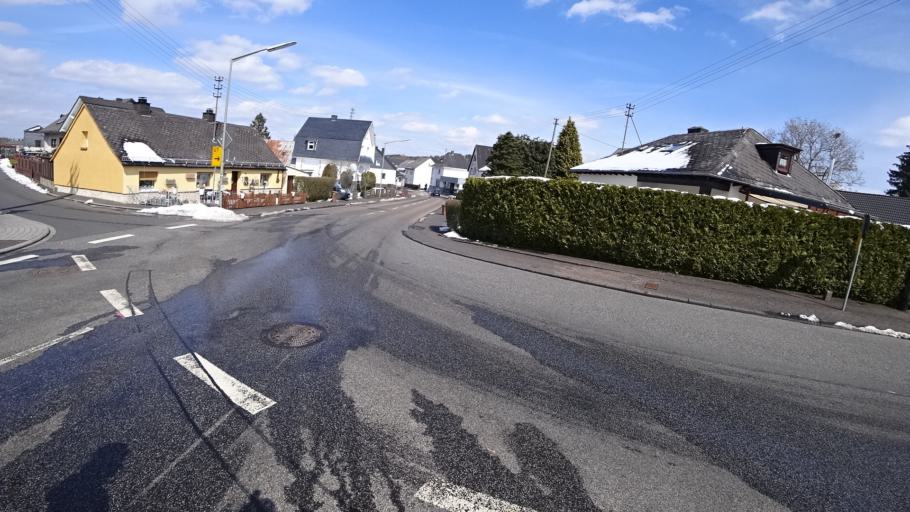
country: DE
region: Rheinland-Pfalz
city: Elkenroth
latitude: 50.7258
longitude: 7.8832
